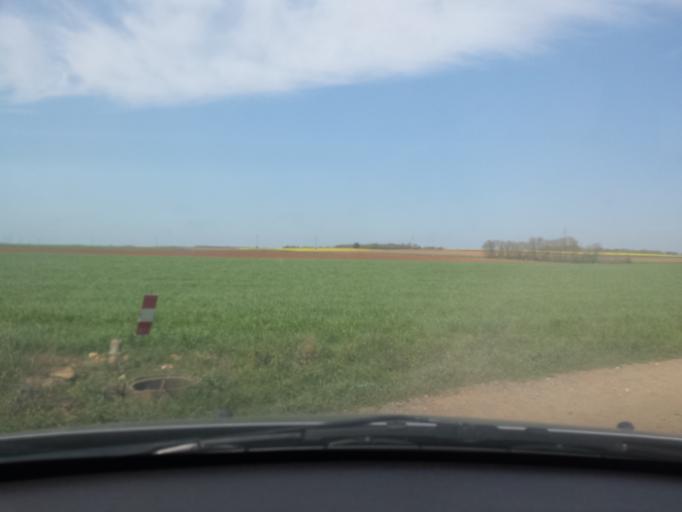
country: FR
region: Pays de la Loire
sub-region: Departement de la Vendee
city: Sainte-Gemme-la-Plaine
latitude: 46.4904
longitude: -1.0826
